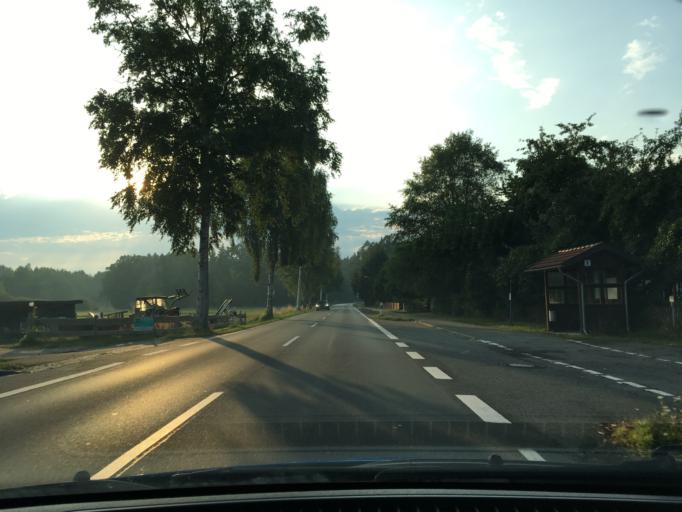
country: DE
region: Lower Saxony
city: Hermannsburg
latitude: 52.7366
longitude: 10.0796
